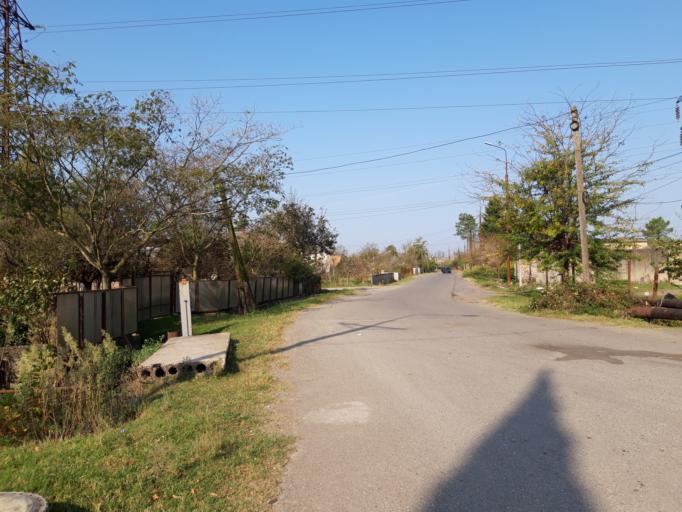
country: GE
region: Imereti
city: Samtredia
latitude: 42.1617
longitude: 42.3268
